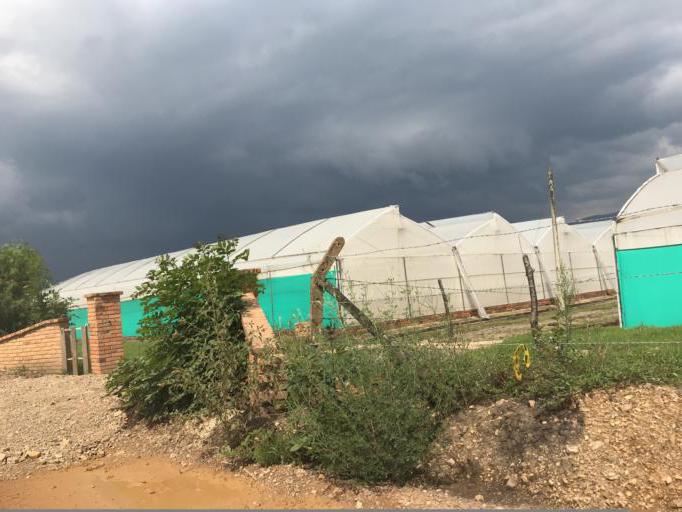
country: CO
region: Boyaca
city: Villa de Leiva
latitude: 5.6590
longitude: -73.5855
